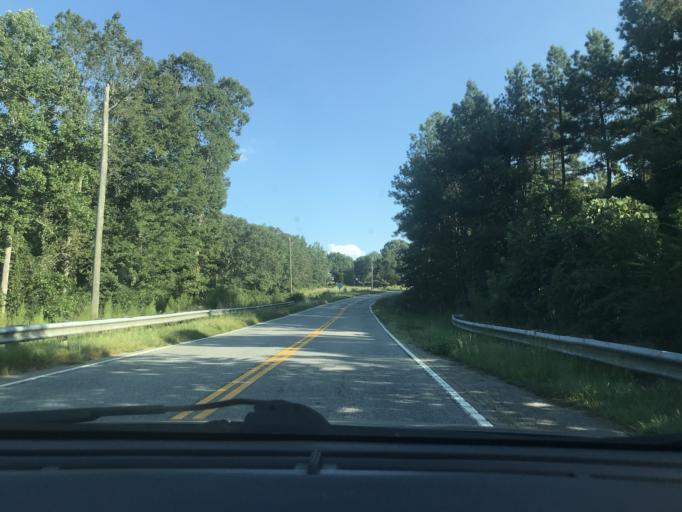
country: US
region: South Carolina
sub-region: Cherokee County
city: Gaffney
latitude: 35.1186
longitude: -81.6801
